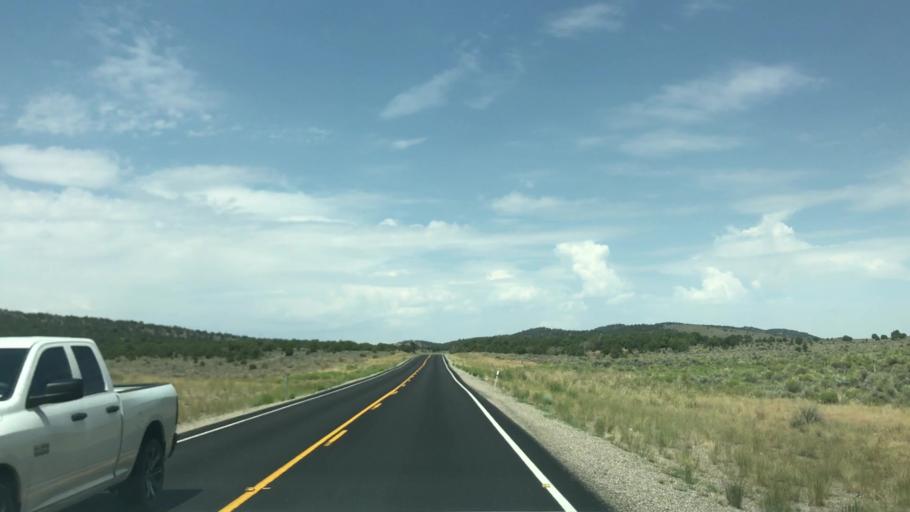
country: US
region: Nevada
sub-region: Eureka County
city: Eureka
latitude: 39.3896
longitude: -115.4505
